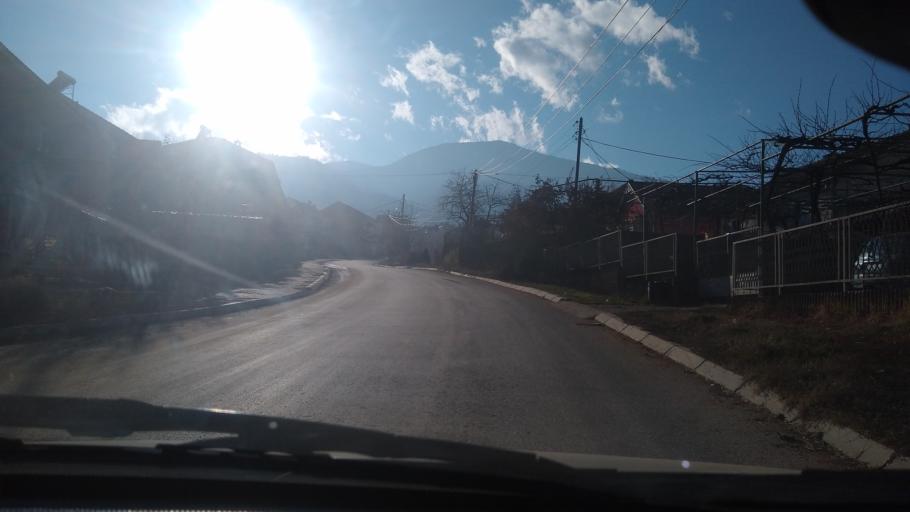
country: MK
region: Bitola
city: Bitola
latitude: 41.0202
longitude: 21.3163
